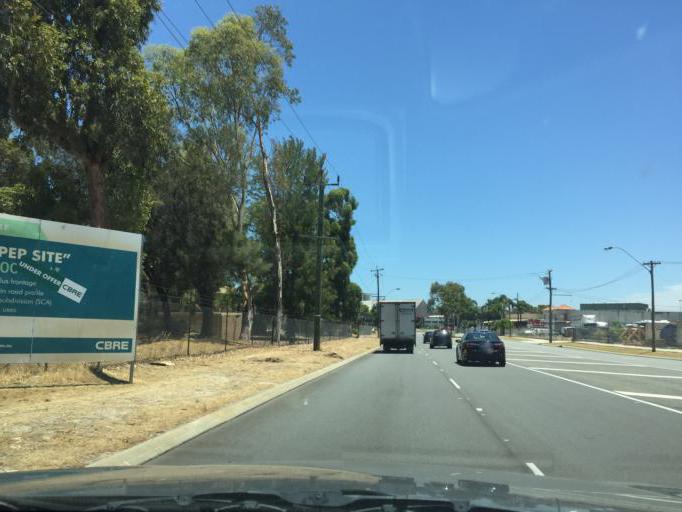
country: AU
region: Western Australia
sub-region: Canning
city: Canning Vale
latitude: -32.0599
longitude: 115.9210
